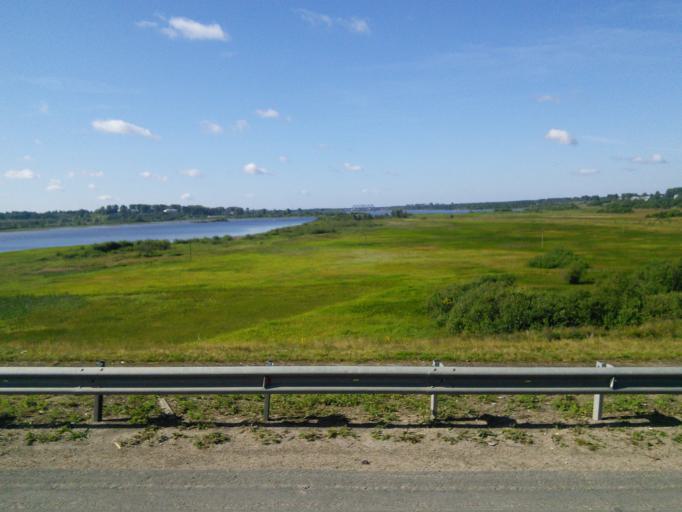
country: RU
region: Vologda
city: Sheksna
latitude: 59.2153
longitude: 38.4909
